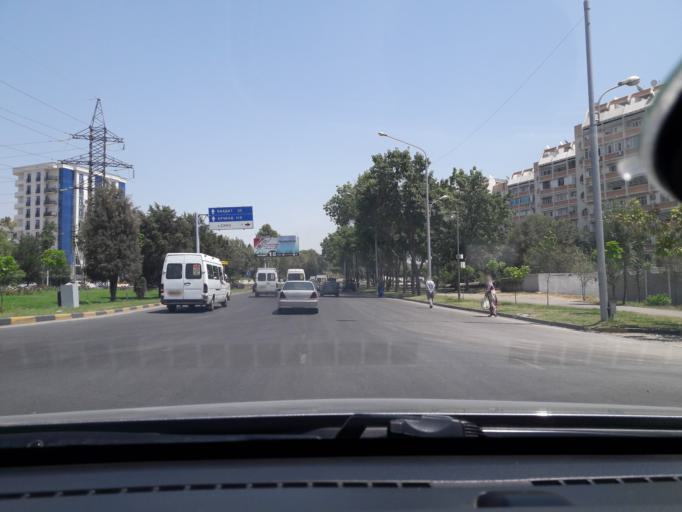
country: TJ
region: Dushanbe
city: Dushanbe
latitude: 38.5910
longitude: 68.7427
